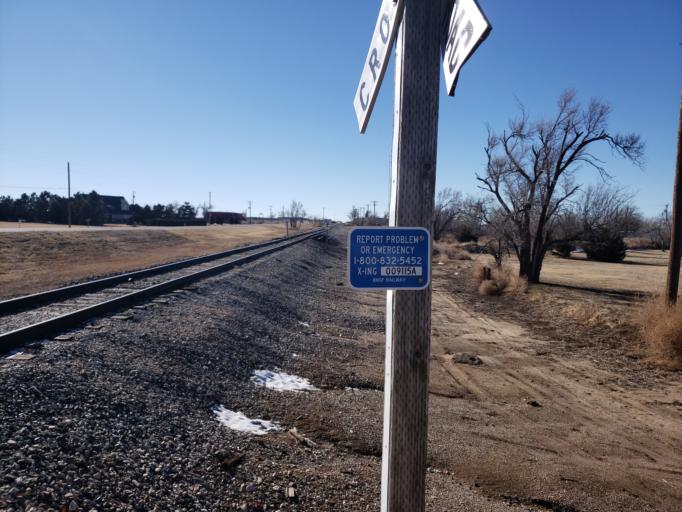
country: US
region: Kansas
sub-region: Ford County
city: Dodge City
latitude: 37.7313
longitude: -100.0438
